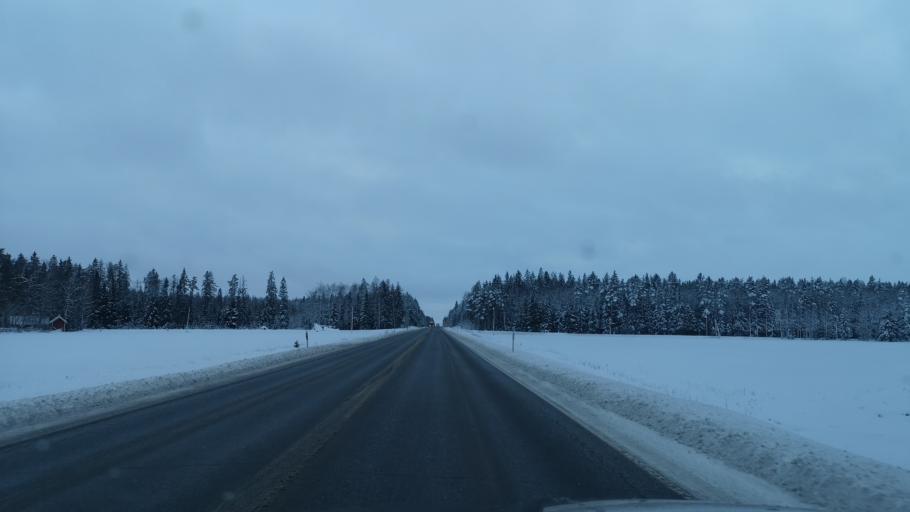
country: FI
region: Varsinais-Suomi
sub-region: Loimaa
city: Loimaa
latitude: 60.9059
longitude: 23.1542
